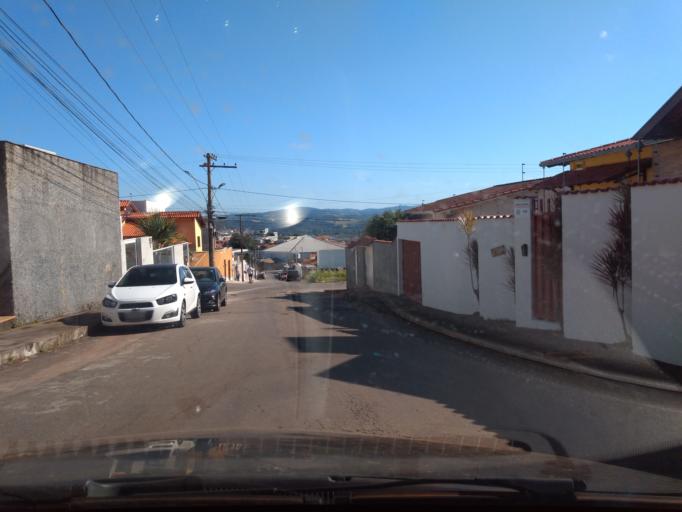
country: BR
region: Minas Gerais
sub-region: Tres Coracoes
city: Tres Coracoes
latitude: -21.6883
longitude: -45.2640
